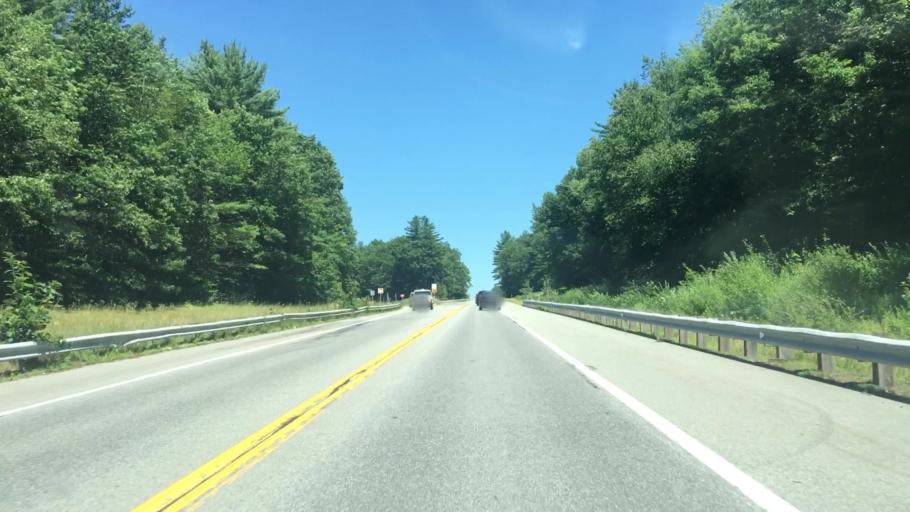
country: US
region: New Hampshire
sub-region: Merrimack County
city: Hopkinton
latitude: 43.1786
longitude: -71.6899
